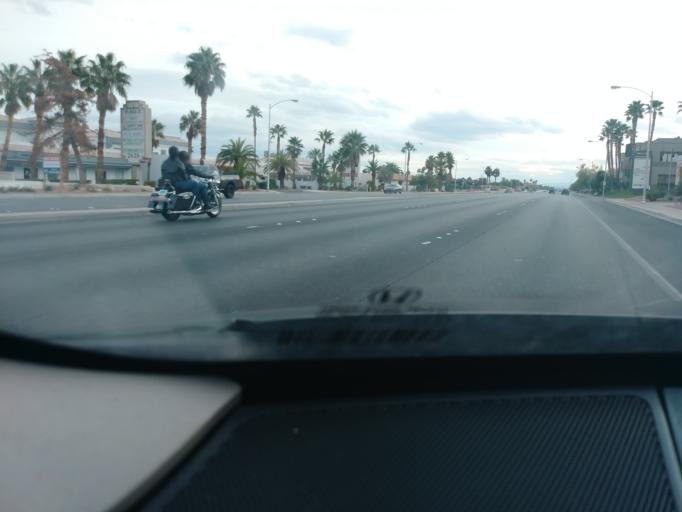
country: US
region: Nevada
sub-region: Clark County
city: Spring Valley
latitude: 36.1422
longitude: -115.2431
